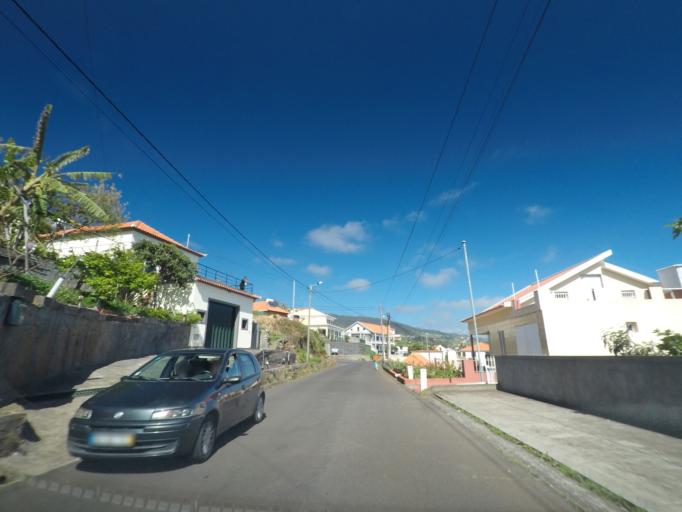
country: PT
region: Madeira
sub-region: Calheta
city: Arco da Calheta
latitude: 32.7004
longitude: -17.1180
